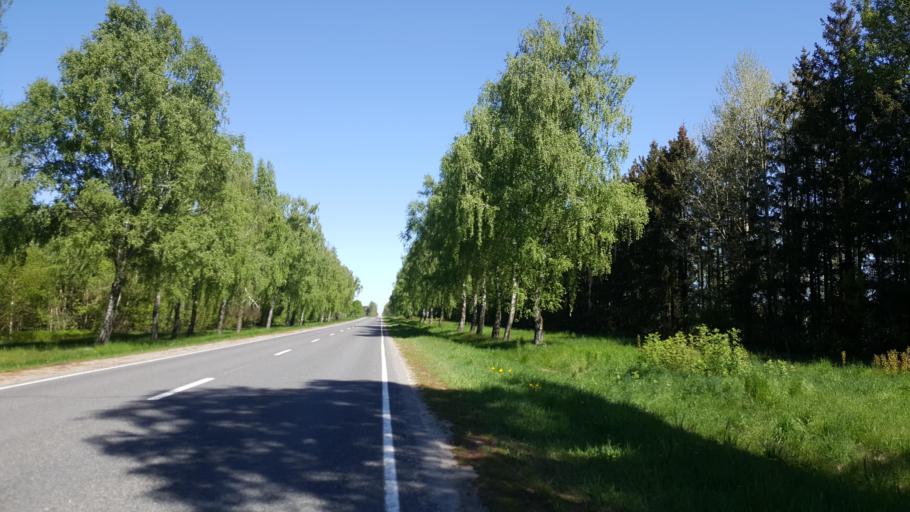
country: BY
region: Brest
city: Kamyanyets
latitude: 52.4631
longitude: 23.7819
